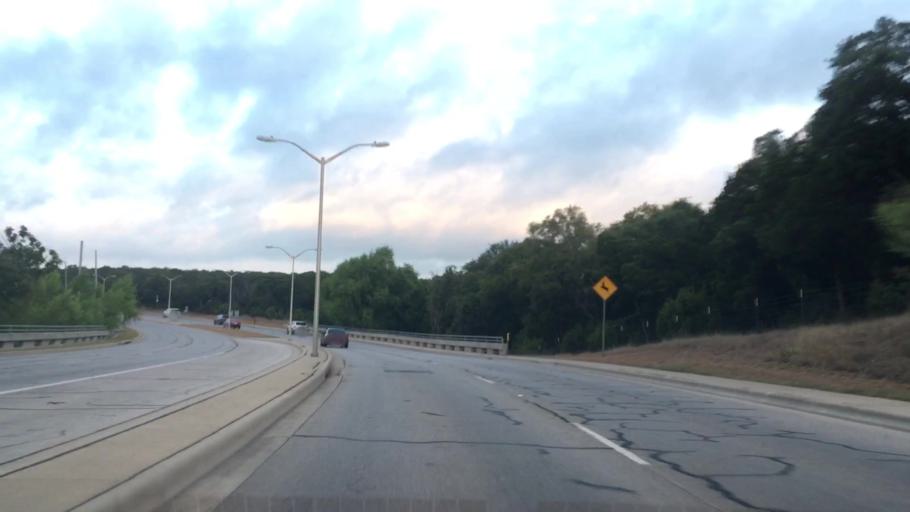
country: US
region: Texas
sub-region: Williamson County
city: Cedar Park
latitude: 30.5091
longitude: -97.7905
